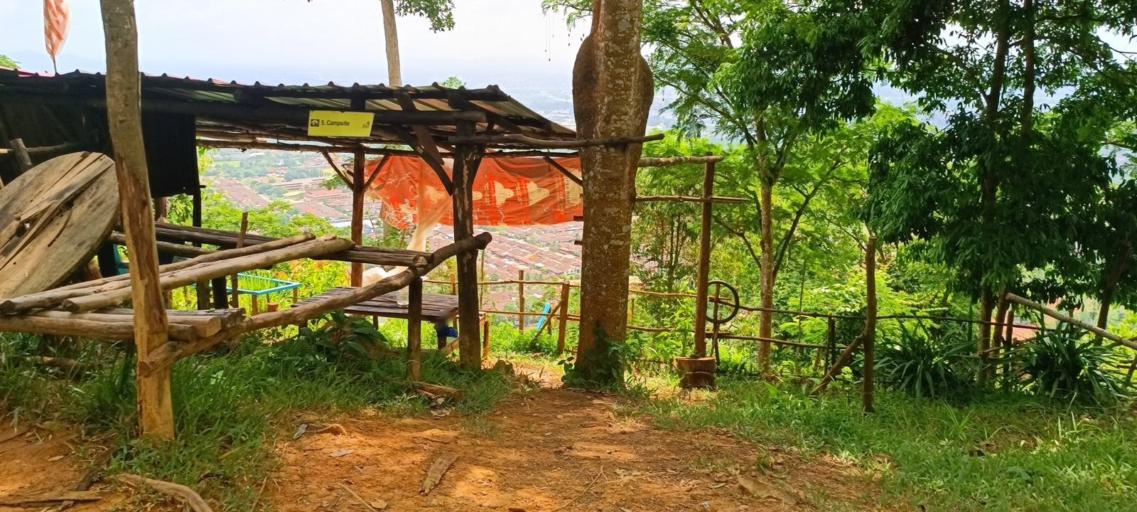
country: MY
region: Kedah
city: Sungai Petani
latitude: 5.6035
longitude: 100.4572
